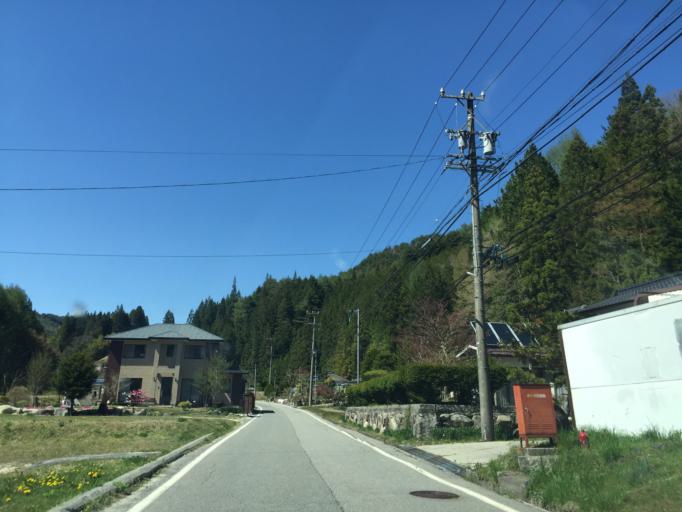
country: JP
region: Nagano
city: Iida
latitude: 35.3822
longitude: 137.6869
